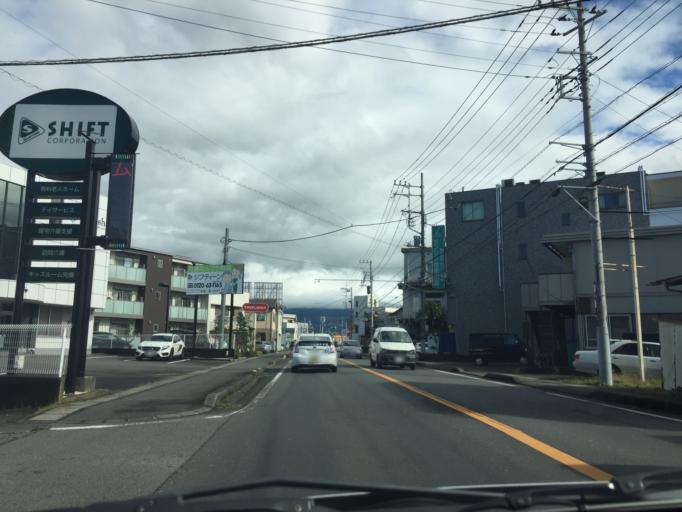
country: JP
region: Shizuoka
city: Mishima
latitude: 35.1141
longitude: 138.8991
